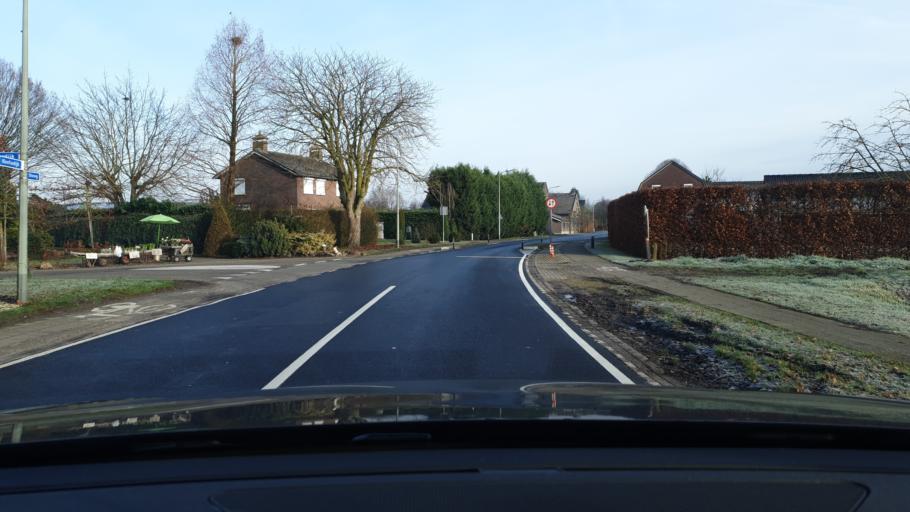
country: NL
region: Limburg
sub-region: Gemeente Peel en Maas
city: Maasbree
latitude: 51.3945
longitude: 6.0148
